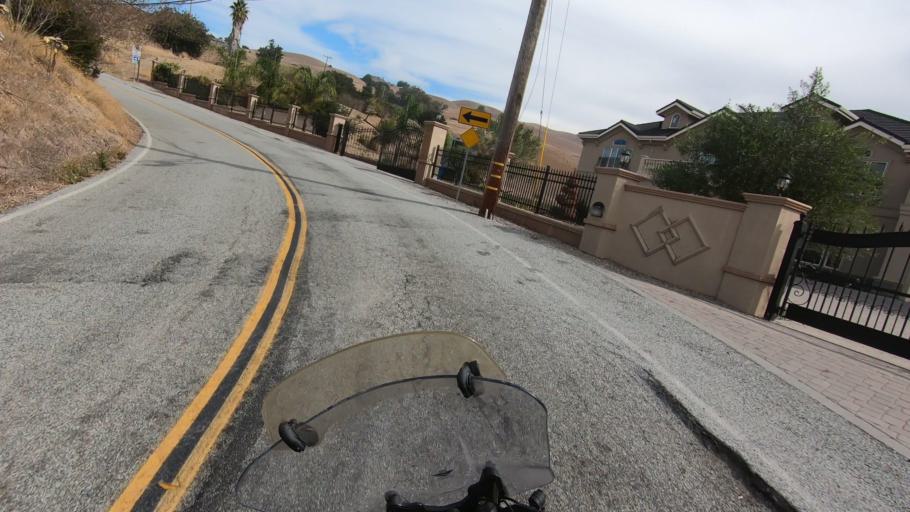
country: US
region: California
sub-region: Santa Clara County
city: East Foothills
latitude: 37.4068
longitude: -121.8359
